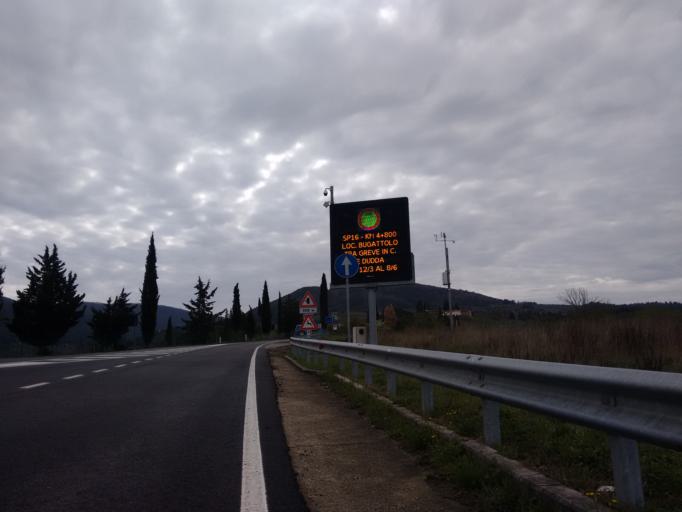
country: IT
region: Tuscany
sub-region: Province of Florence
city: Strada in Chianti
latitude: 43.6519
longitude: 11.3083
